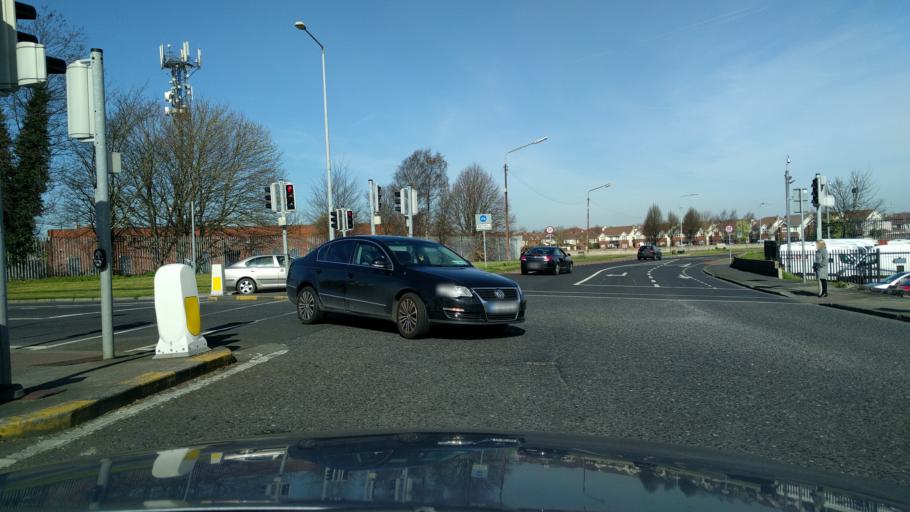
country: IE
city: Palmerstown
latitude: 53.3455
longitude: -6.3795
